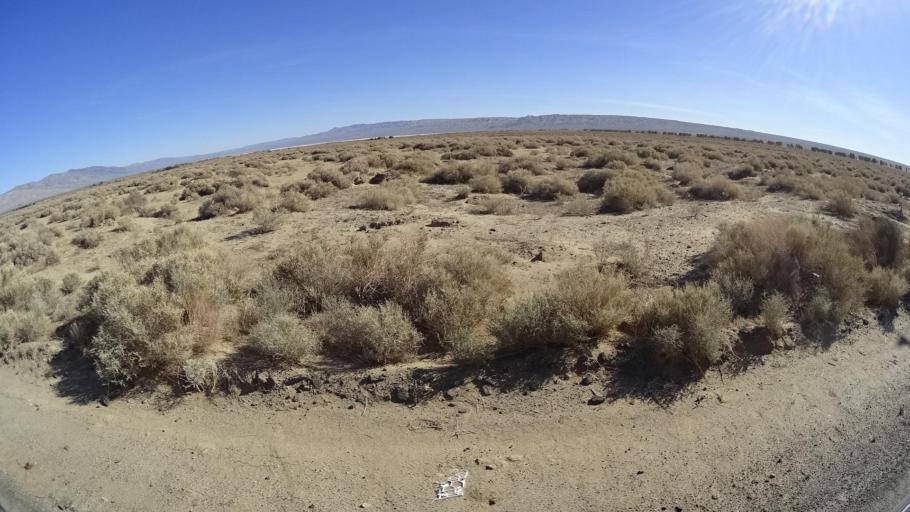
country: US
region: California
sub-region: Kern County
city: California City
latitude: 35.2920
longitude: -117.9681
